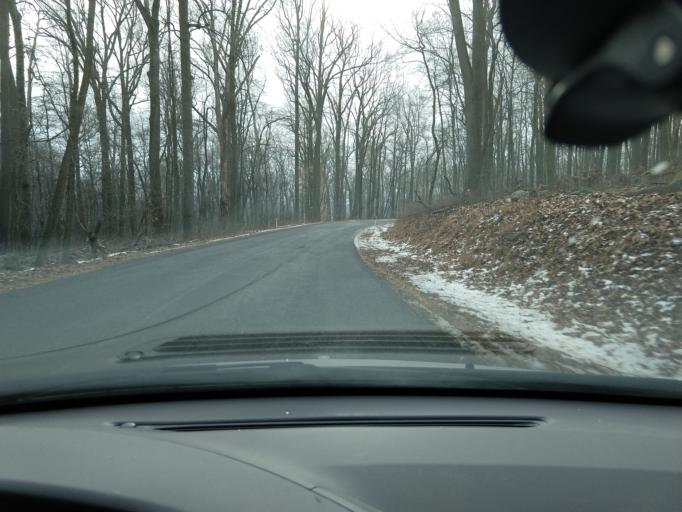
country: US
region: Pennsylvania
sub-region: Berks County
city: Birdsboro
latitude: 40.2119
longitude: -75.7740
